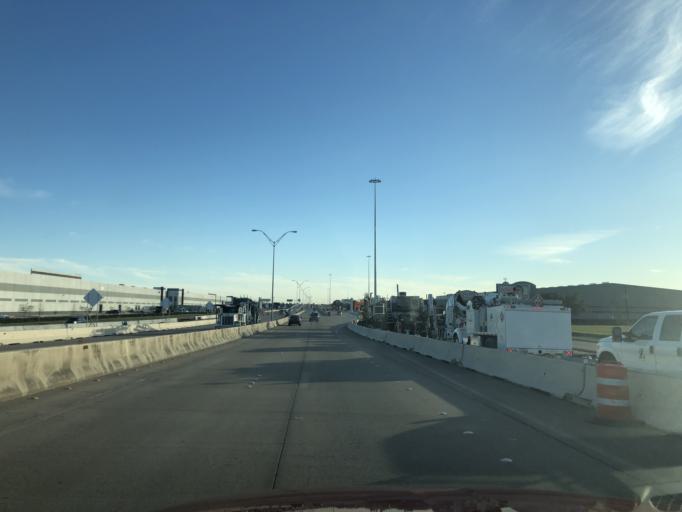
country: US
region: Texas
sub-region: Harris County
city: Deer Park
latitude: 29.6991
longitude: -95.1536
